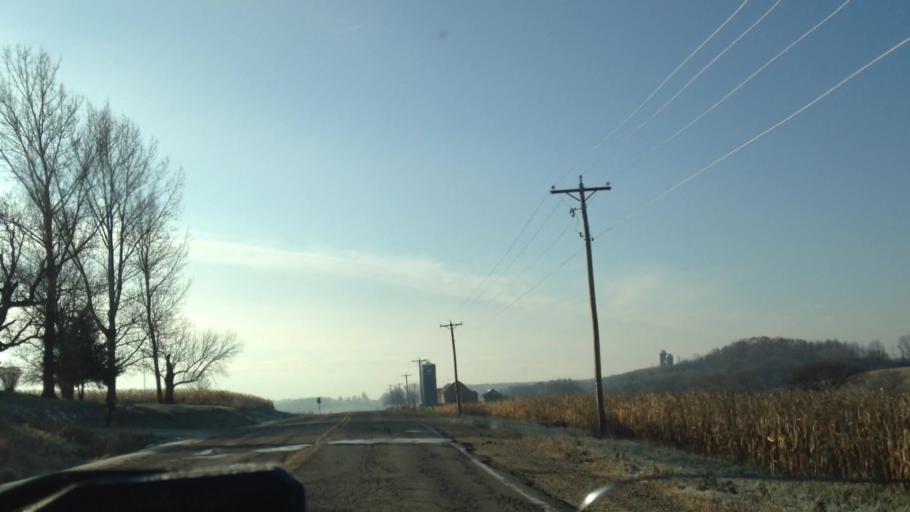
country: US
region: Wisconsin
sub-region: Dodge County
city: Mayville
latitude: 43.4768
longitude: -88.4999
